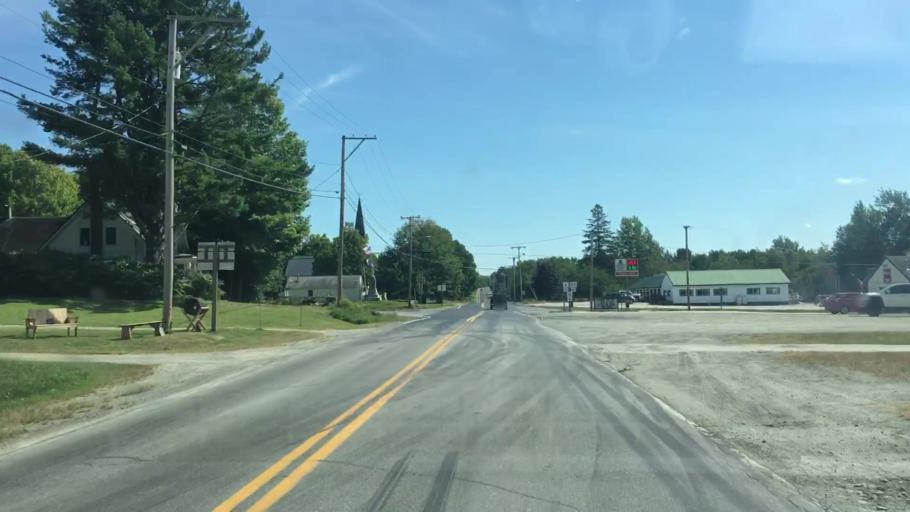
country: US
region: Maine
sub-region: Penobscot County
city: Bradford
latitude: 45.1673
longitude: -68.8454
